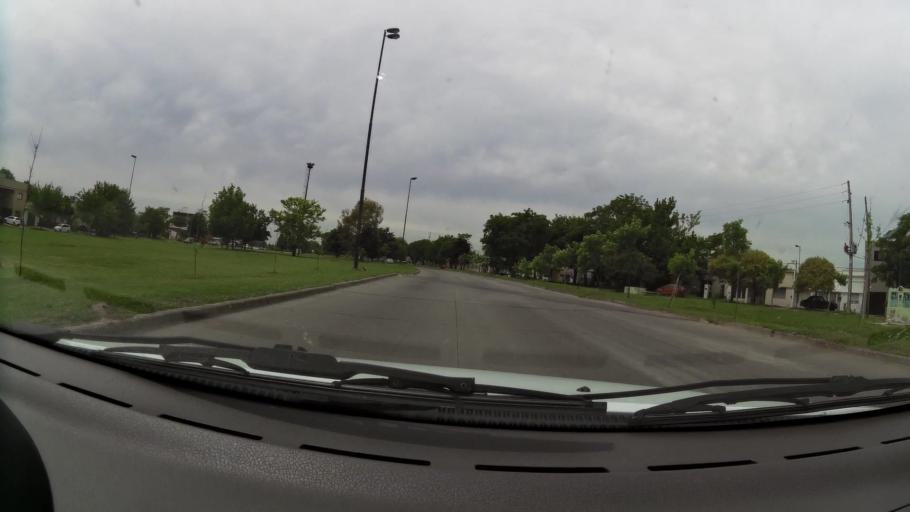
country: AR
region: Buenos Aires
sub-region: Partido de La Plata
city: La Plata
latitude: -34.9498
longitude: -57.9479
